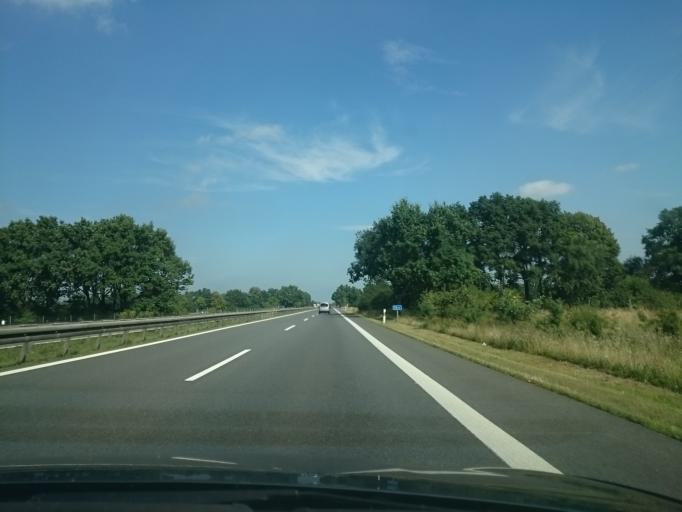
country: DE
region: Brandenburg
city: Calau
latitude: 51.7633
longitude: 13.8651
